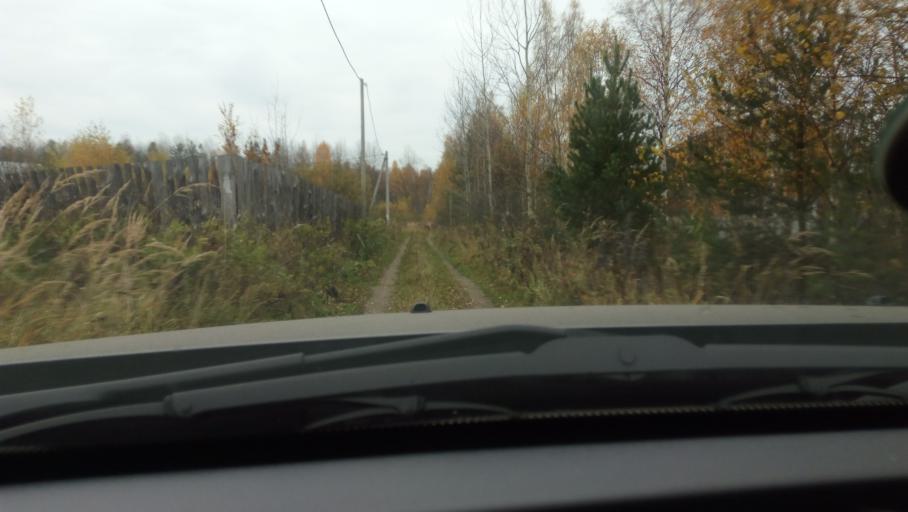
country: RU
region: Moskovskaya
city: Avsyunino
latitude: 55.5794
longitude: 39.2492
